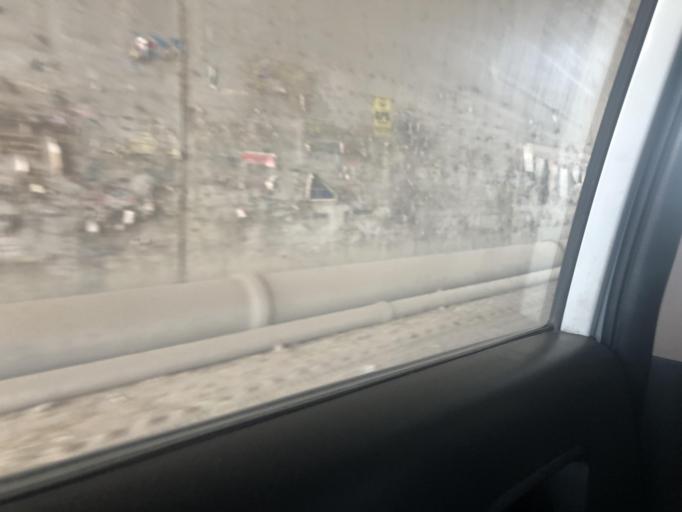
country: IN
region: Haryana
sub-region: Jhajjar
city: Bahadurgarh
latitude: 28.6873
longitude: 76.8841
